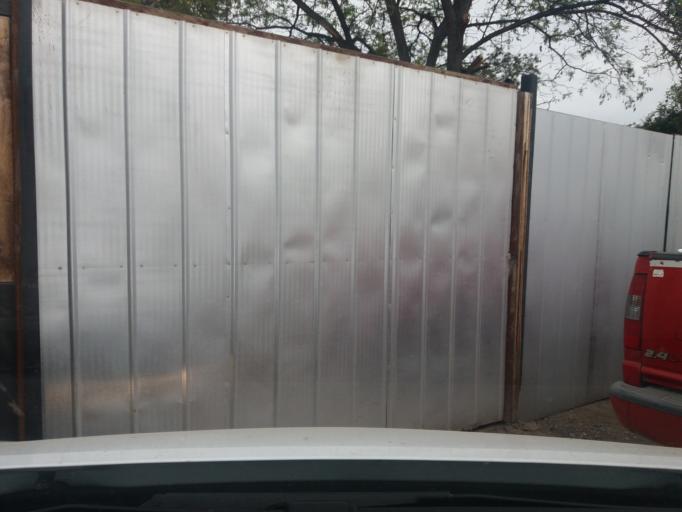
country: CL
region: Valparaiso
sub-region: Provincia de Los Andes
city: Los Andes
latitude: -32.8453
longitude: -70.6374
